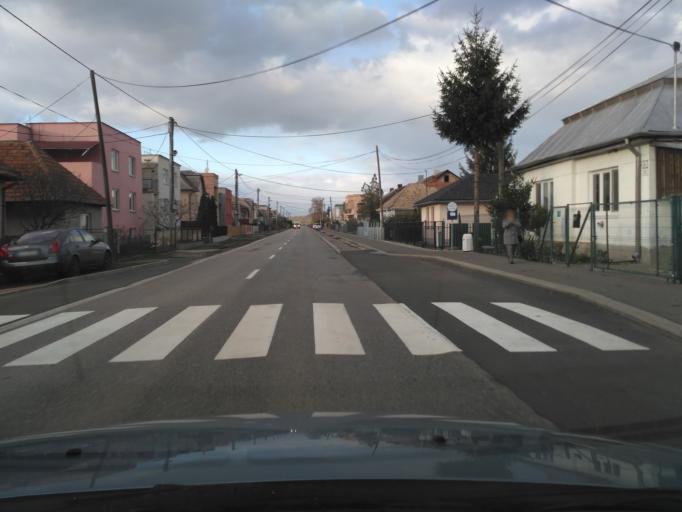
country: HU
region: Borsod-Abauj-Zemplen
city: Satoraljaujhely
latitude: 48.4076
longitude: 21.6683
